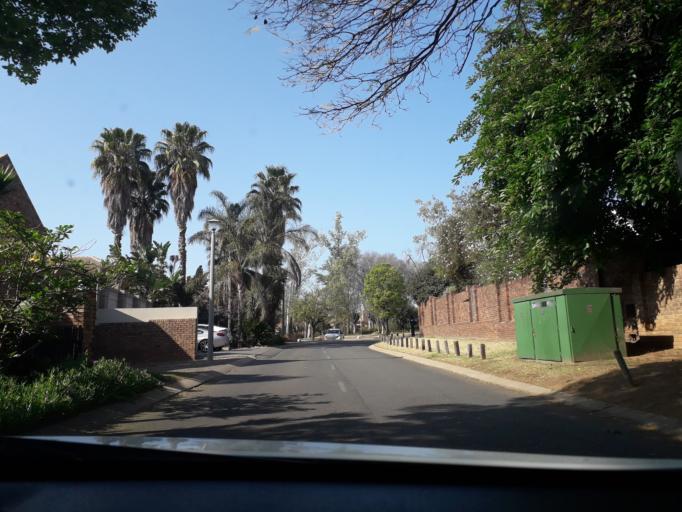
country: ZA
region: Gauteng
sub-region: Ekurhuleni Metropolitan Municipality
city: Tembisa
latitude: -26.0644
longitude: 28.2502
